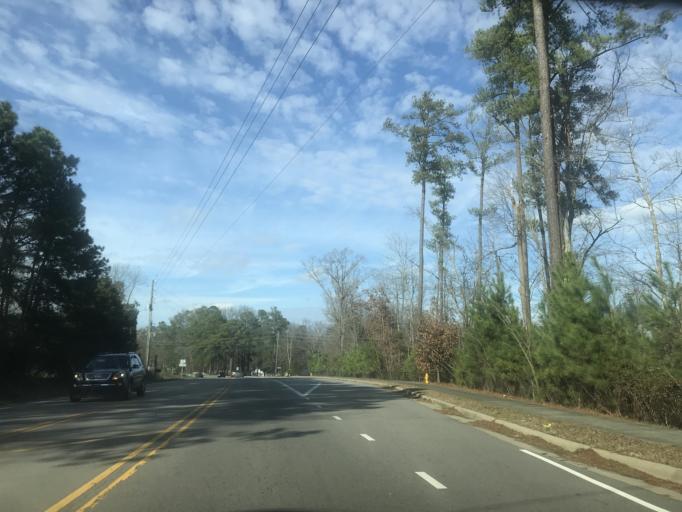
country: US
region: North Carolina
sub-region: Wake County
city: Garner
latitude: 35.7245
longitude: -78.5492
